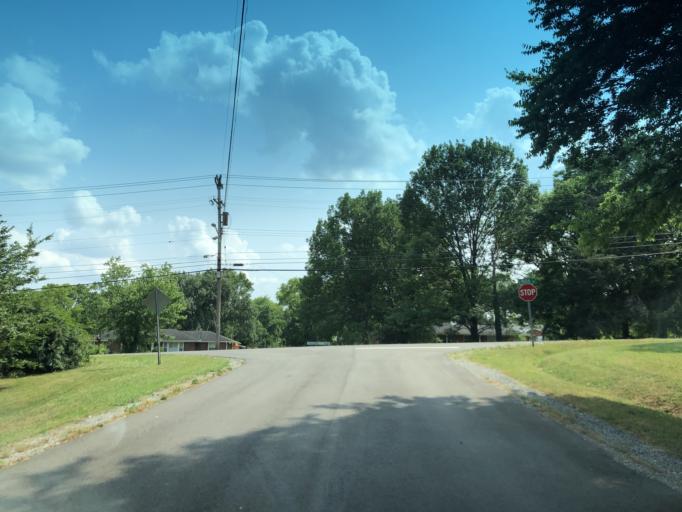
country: US
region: Tennessee
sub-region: Davidson County
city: Goodlettsville
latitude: 36.2615
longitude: -86.7198
